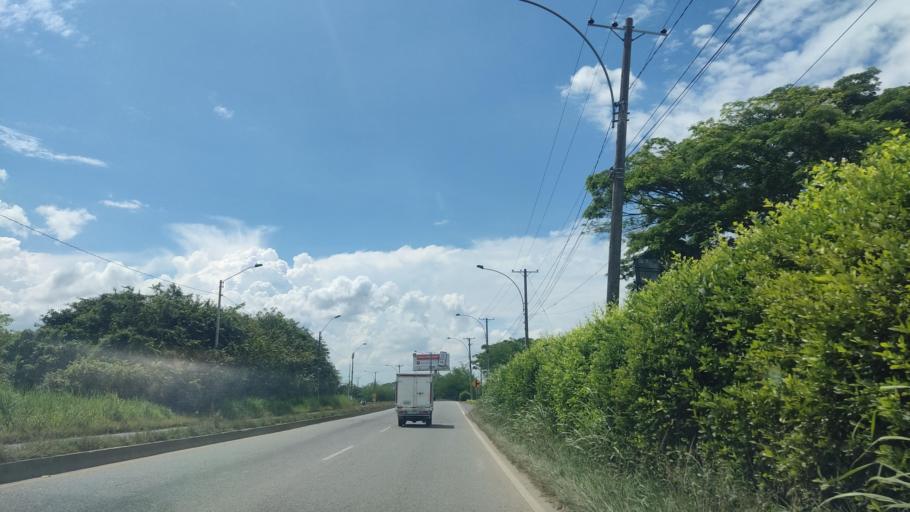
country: CO
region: Valle del Cauca
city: Jamundi
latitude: 3.3049
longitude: -76.5214
